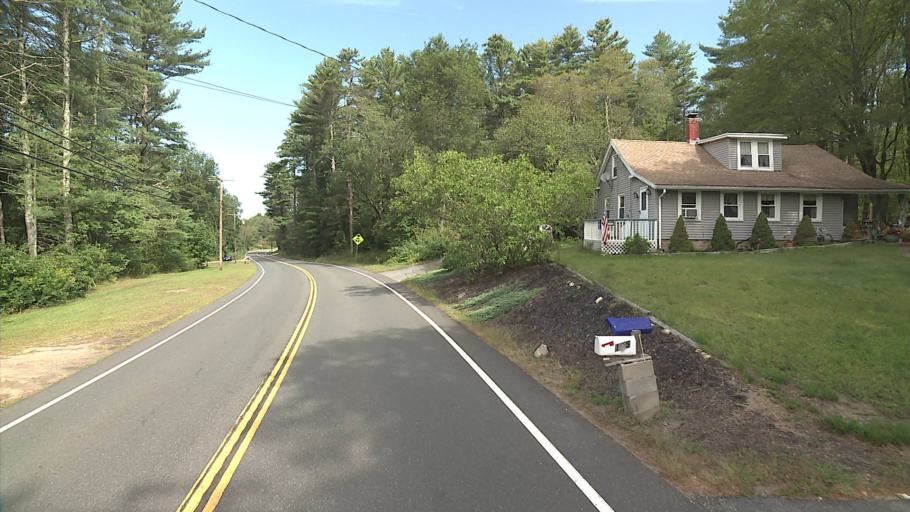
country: US
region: Connecticut
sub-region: Tolland County
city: Stafford
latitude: 41.9851
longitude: -72.3163
